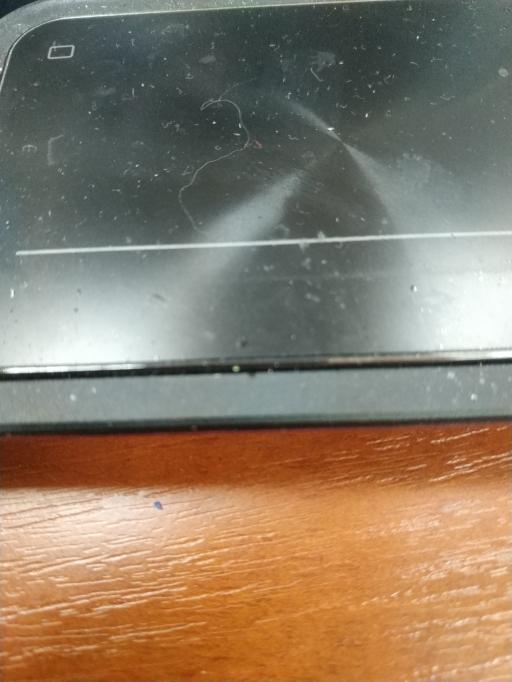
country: RU
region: Tula
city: Zaokskiy
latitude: 54.7270
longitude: 37.4834
